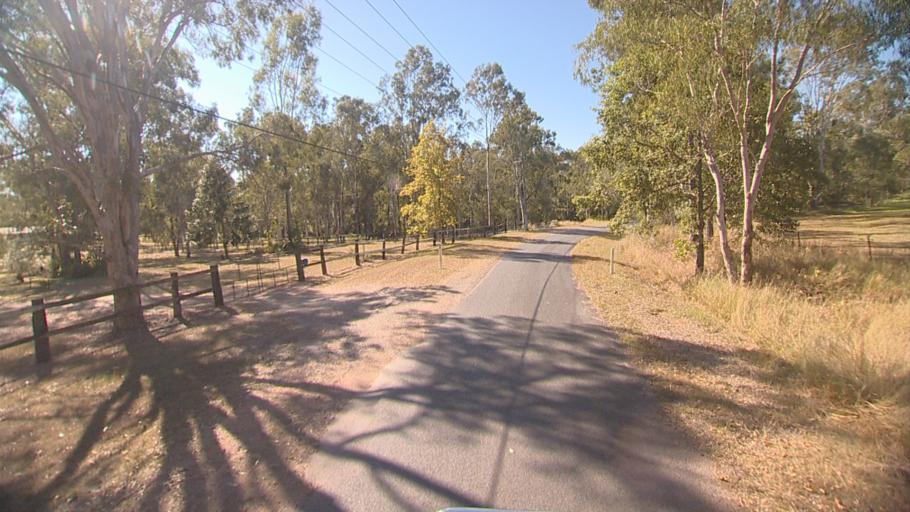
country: AU
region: Queensland
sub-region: Logan
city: North Maclean
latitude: -27.7646
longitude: 153.0247
